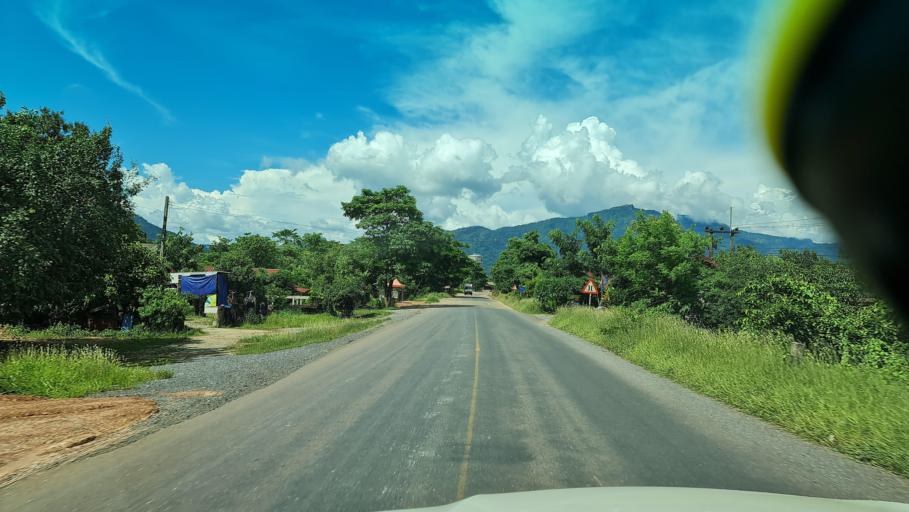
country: LA
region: Bolikhamxai
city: Pakkading
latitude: 18.2995
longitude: 104.1084
